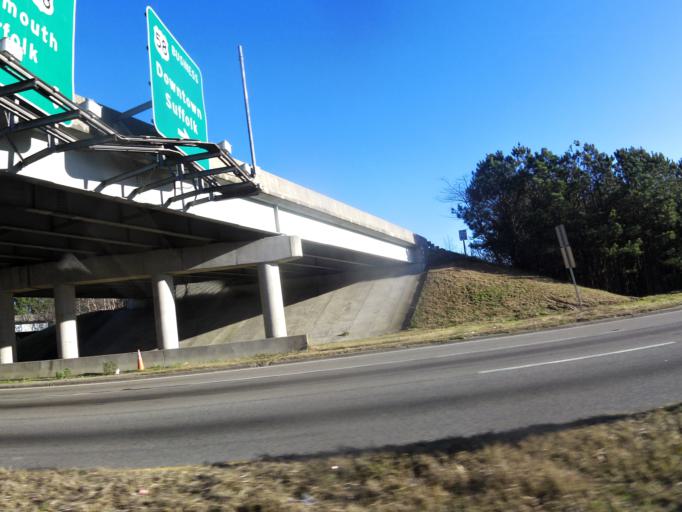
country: US
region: Virginia
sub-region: City of Suffolk
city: South Suffolk
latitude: 36.7265
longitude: -76.6324
